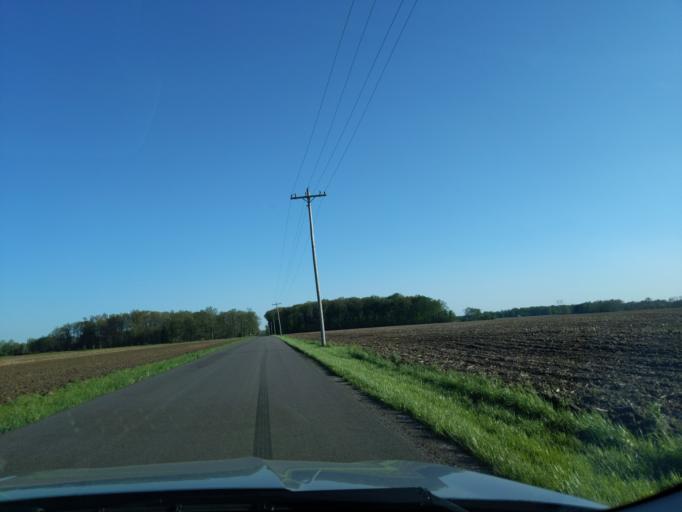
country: US
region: Indiana
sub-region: Decatur County
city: Westport
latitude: 39.1975
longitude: -85.5458
